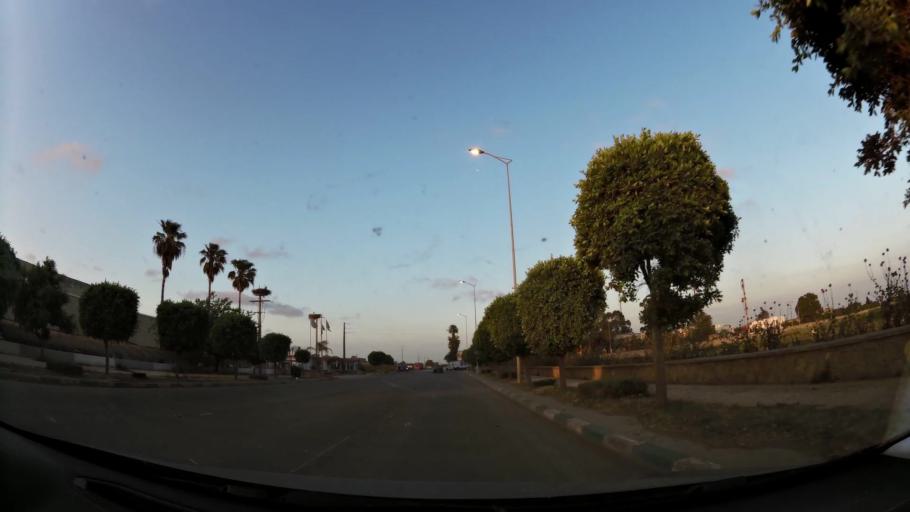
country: MA
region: Gharb-Chrarda-Beni Hssen
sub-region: Kenitra Province
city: Kenitra
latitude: 34.2791
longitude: -6.5446
